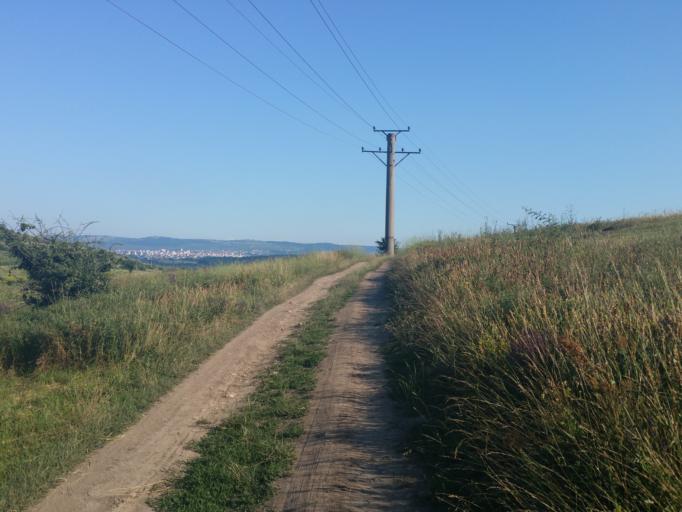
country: RO
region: Cluj
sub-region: Comuna Baciu
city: Baciu
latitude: 46.8045
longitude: 23.5295
